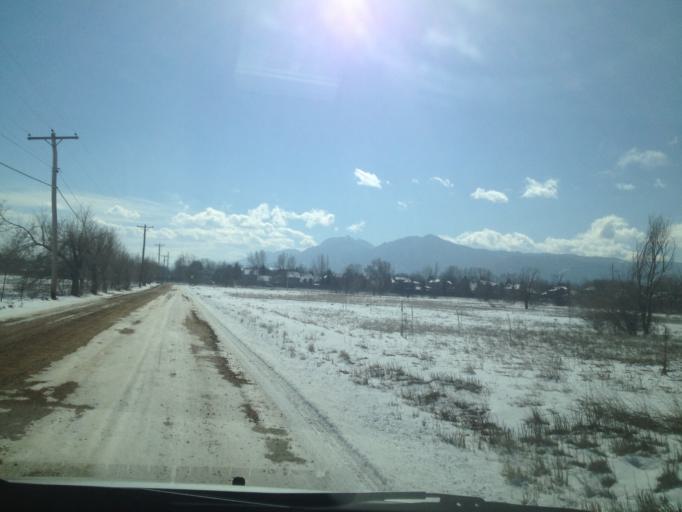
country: US
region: Colorado
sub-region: Boulder County
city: Boulder
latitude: 40.0564
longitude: -105.2634
